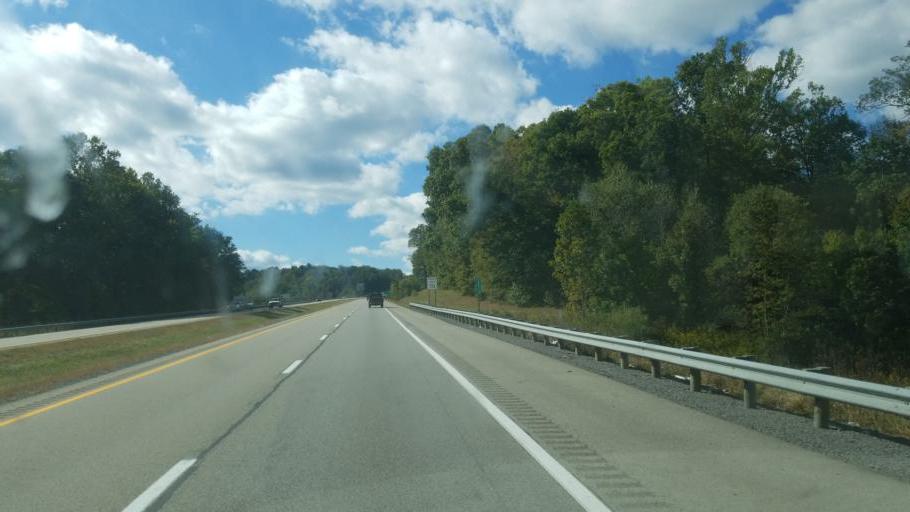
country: US
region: West Virginia
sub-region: Preston County
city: Kingwood
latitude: 39.6562
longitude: -79.6487
